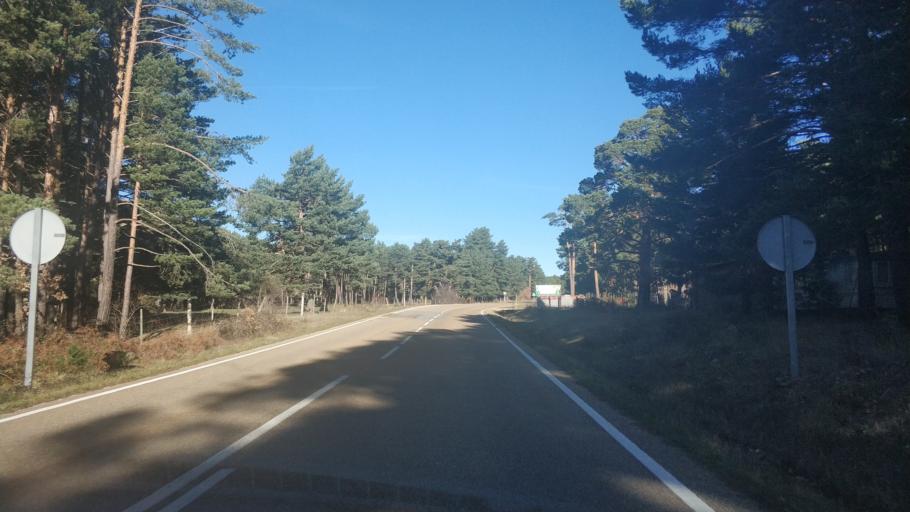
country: ES
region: Castille and Leon
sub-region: Provincia de Soria
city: Vinuesa
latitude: 41.9253
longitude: -2.7632
